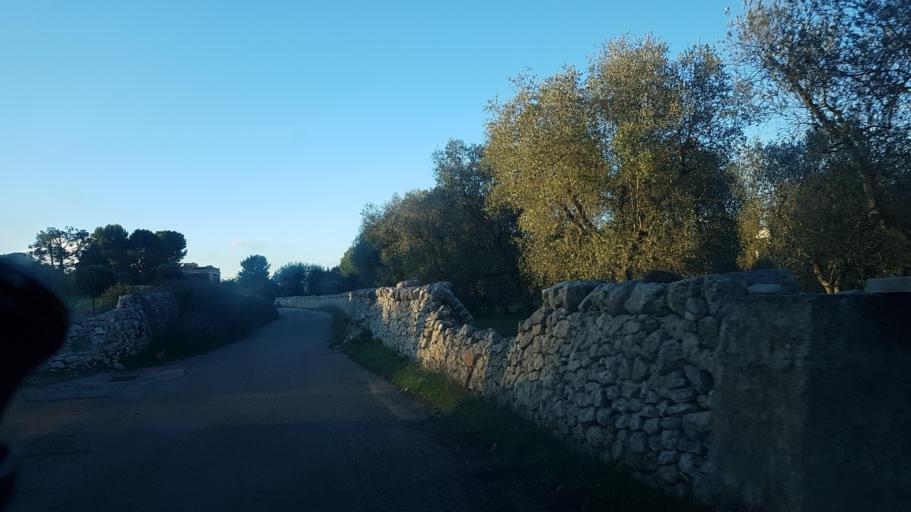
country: IT
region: Apulia
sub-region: Provincia di Brindisi
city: Ostuni
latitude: 40.7048
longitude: 17.5356
